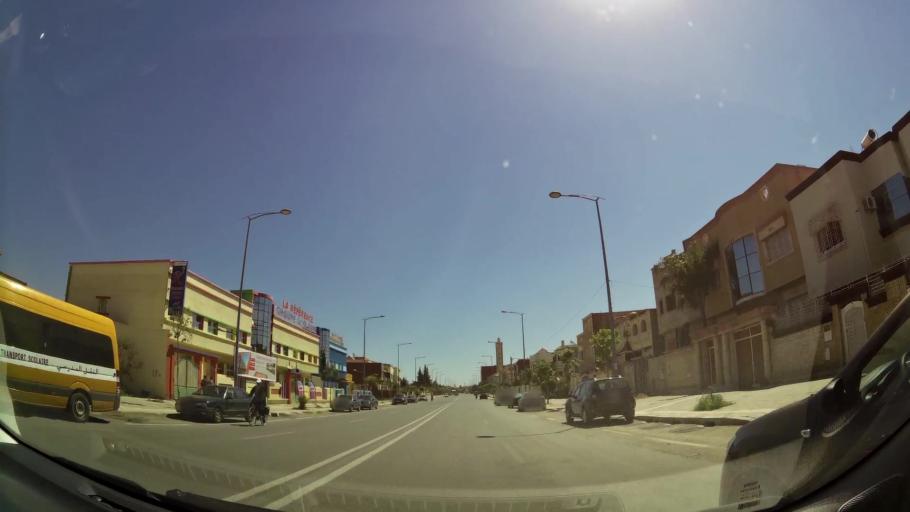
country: MA
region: Oriental
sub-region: Oujda-Angad
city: Oujda
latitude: 34.6666
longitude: -1.8797
